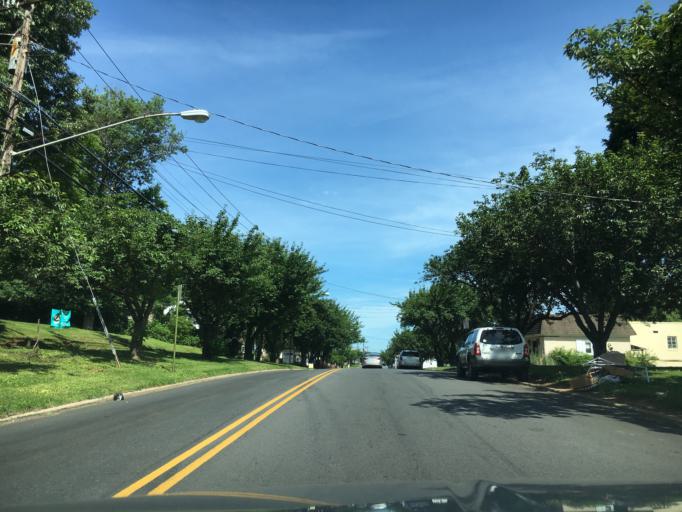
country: US
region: Virginia
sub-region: City of Lynchburg
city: West Lynchburg
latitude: 37.3991
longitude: -79.1716
